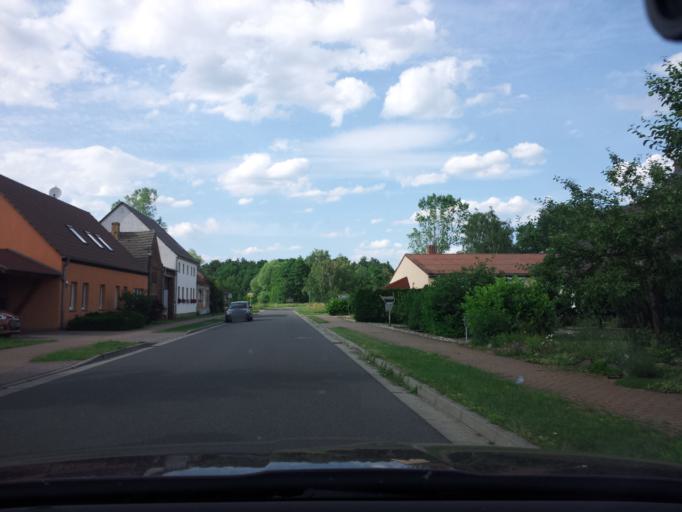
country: DE
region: Brandenburg
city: Juterbog
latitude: 52.0249
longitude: 13.0591
